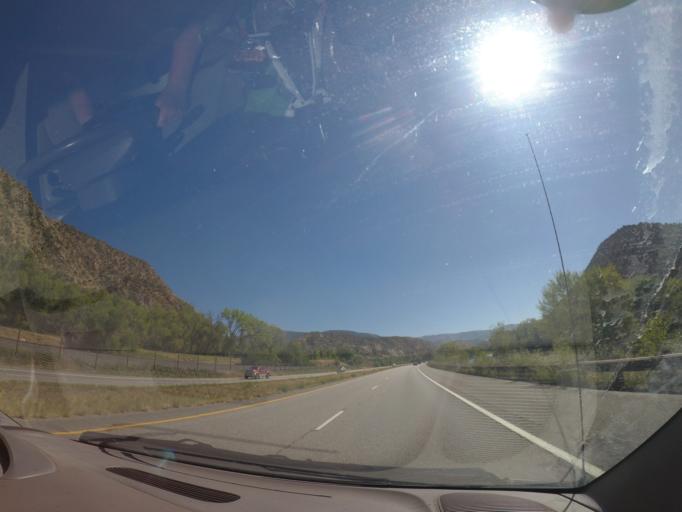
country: US
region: Colorado
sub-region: Garfield County
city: New Castle
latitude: 39.5673
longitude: -107.5471
